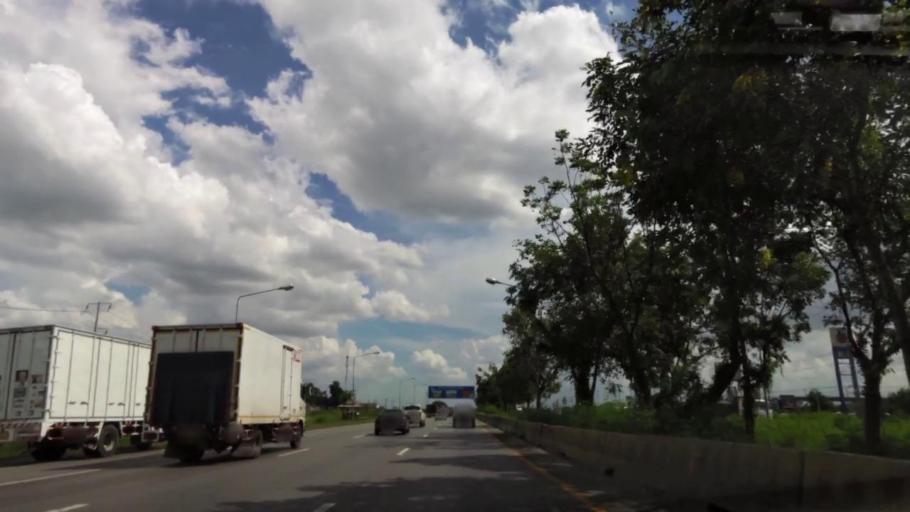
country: TH
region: Phra Nakhon Si Ayutthaya
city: Phra Nakhon Si Ayutthaya
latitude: 14.3964
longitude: 100.5940
